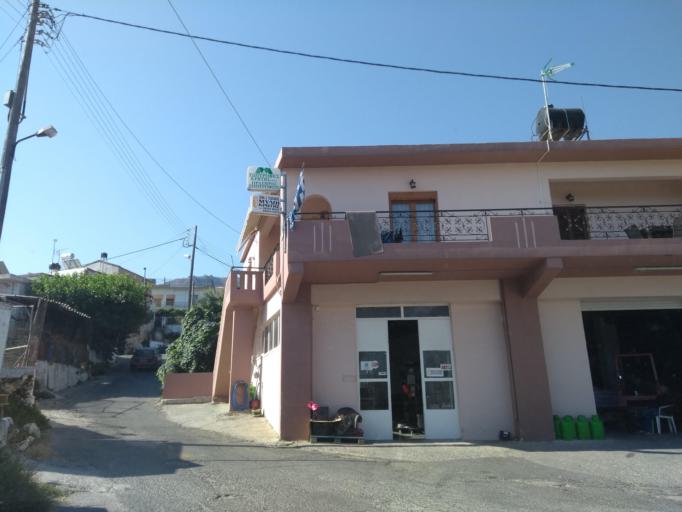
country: GR
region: Crete
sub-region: Nomos Chanias
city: Georgioupolis
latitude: 35.3144
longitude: 24.2953
